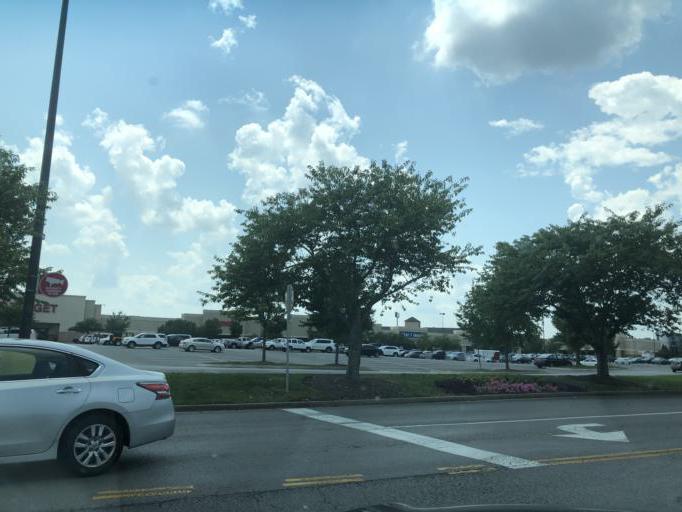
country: US
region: Tennessee
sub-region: Rutherford County
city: Murfreesboro
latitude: 35.8452
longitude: -86.4261
